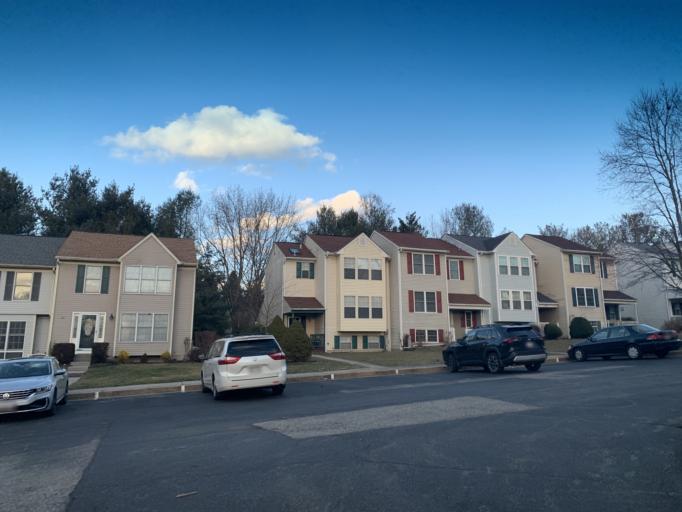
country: US
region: Maryland
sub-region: Harford County
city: South Bel Air
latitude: 39.5339
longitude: -76.3079
